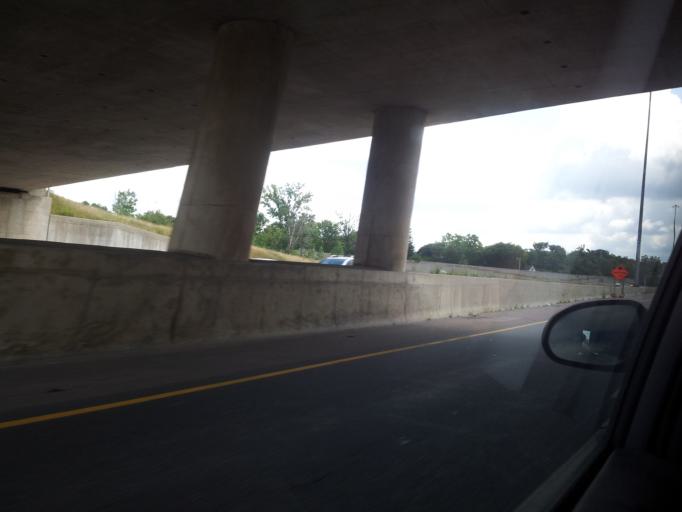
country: CA
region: Ontario
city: Kitchener
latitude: 43.4467
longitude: -80.4610
